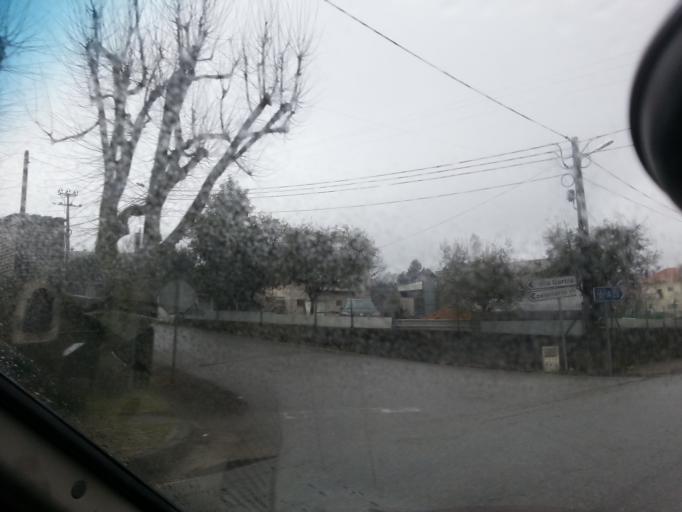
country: PT
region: Viseu
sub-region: Mangualde
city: Mangualde
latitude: 40.6251
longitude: -7.8054
